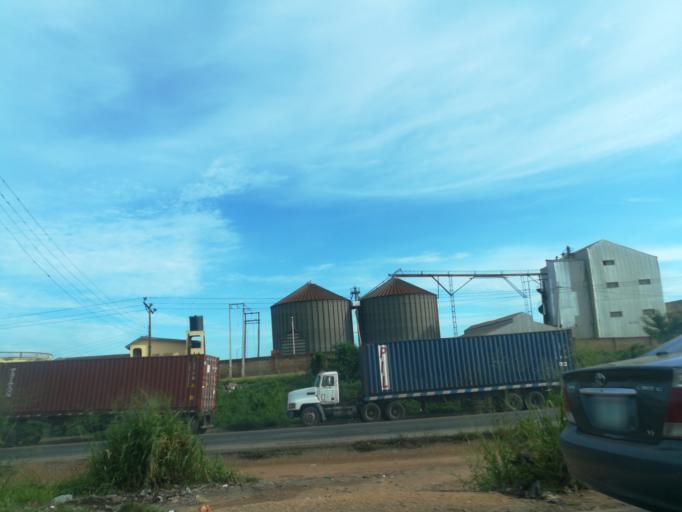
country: NG
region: Oyo
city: Ibadan
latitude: 7.3426
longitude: 3.9097
